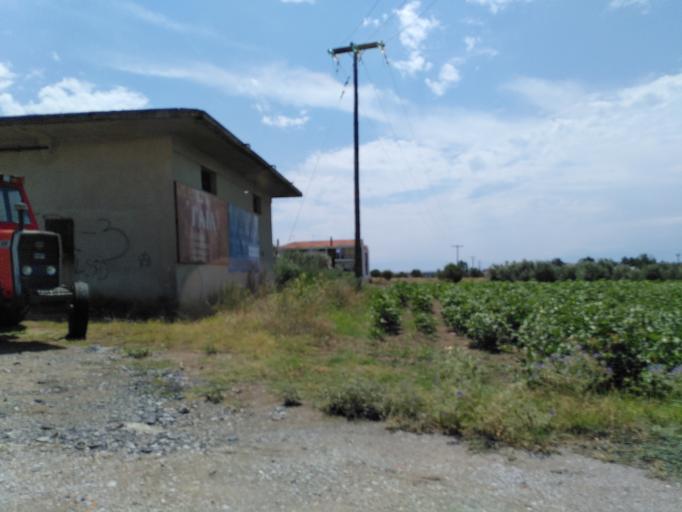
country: GR
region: Central Macedonia
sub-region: Nomos Thessalonikis
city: Epanomi
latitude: 40.4313
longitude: 22.9191
